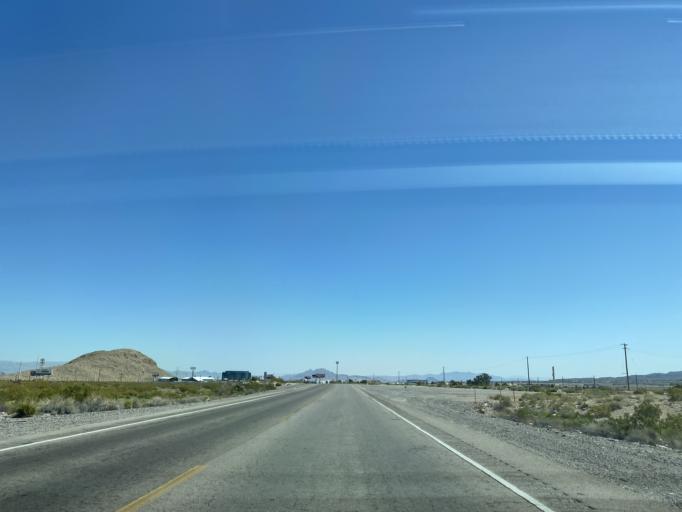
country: US
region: Nevada
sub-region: Clark County
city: Enterprise
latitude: 35.9423
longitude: -115.1823
